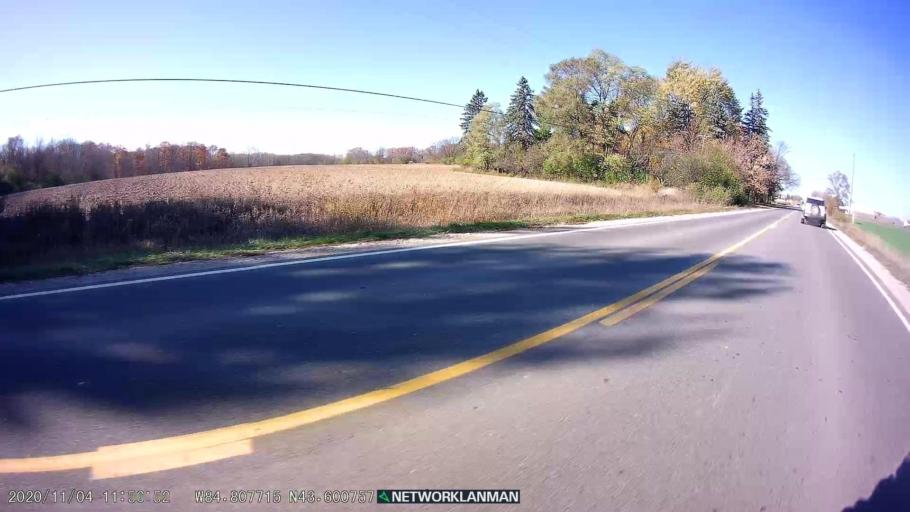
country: US
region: Michigan
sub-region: Isabella County
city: Mount Pleasant
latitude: 43.6006
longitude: -84.8077
